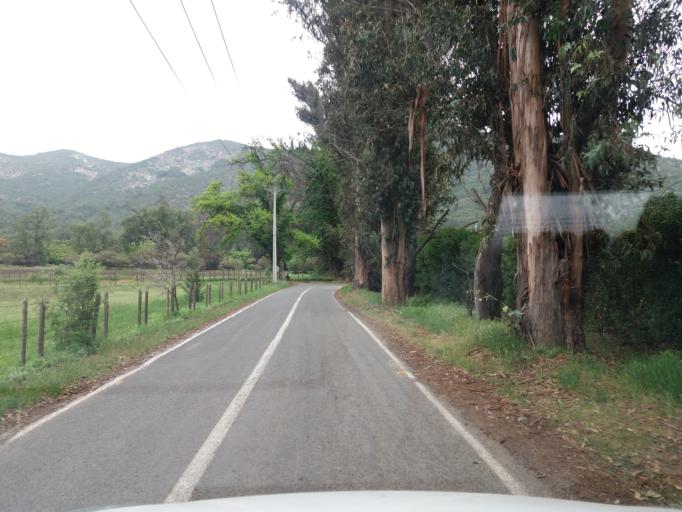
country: CL
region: Valparaiso
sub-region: Provincia de Quillota
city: Quillota
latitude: -32.9076
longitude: -71.1007
